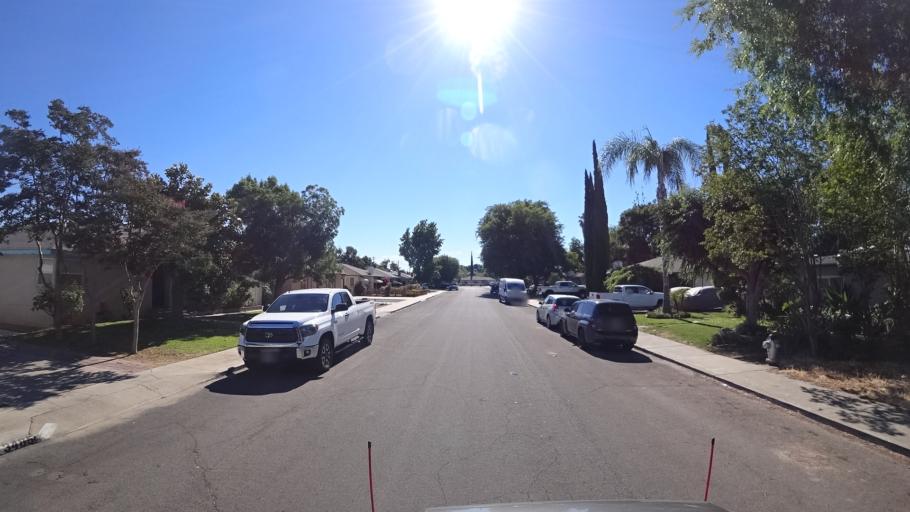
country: US
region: California
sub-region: Fresno County
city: Fresno
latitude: 36.7756
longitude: -119.7660
